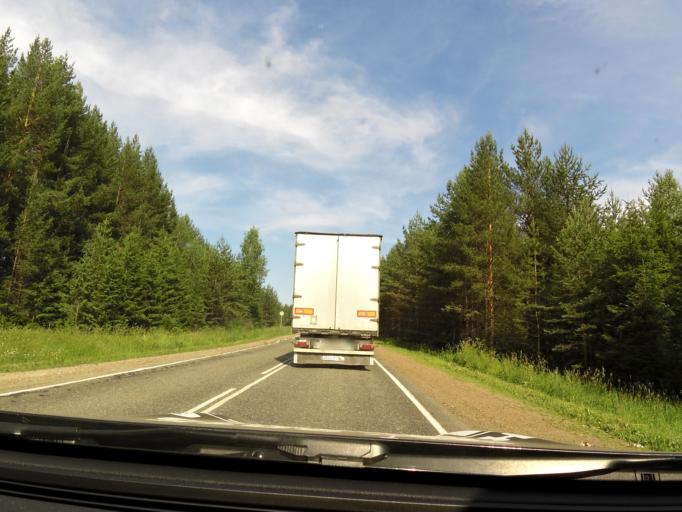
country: RU
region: Kirov
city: Belaya Kholunitsa
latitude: 58.8092
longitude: 50.5711
